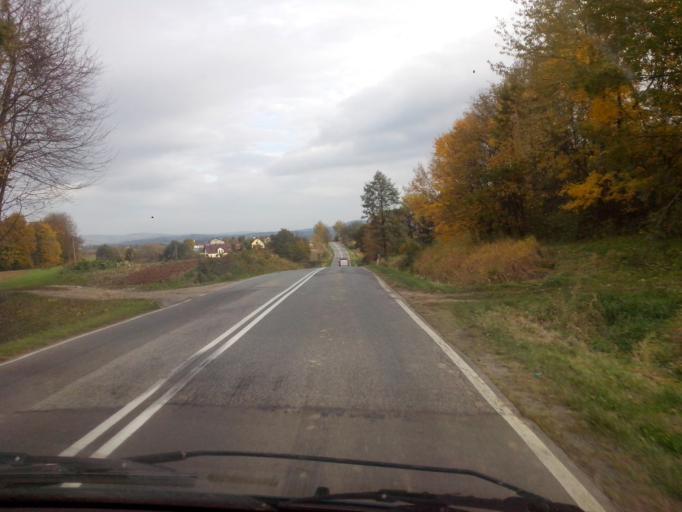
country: PL
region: Subcarpathian Voivodeship
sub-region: Powiat strzyzowski
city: Wisniowa
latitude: 49.8752
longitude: 21.6513
